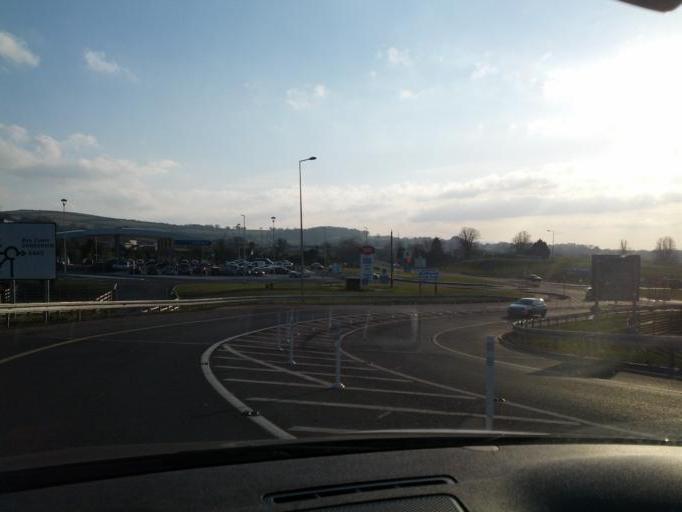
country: IE
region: Munster
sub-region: North Tipperary
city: Templemore
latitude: 52.8859
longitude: -7.9439
